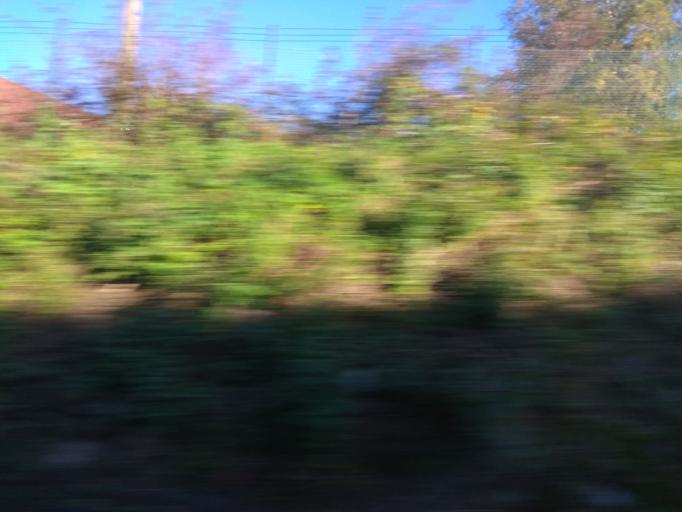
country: FR
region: Rhone-Alpes
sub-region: Departement de la Haute-Savoie
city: Saint-Martin-Bellevue
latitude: 45.9521
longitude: 6.1582
